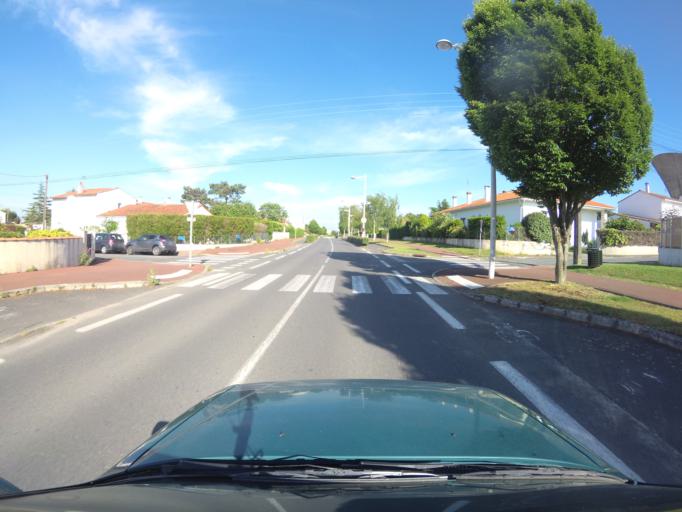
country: FR
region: Poitou-Charentes
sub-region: Departement de la Charente-Maritime
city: Royan
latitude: 45.6354
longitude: -1.0257
